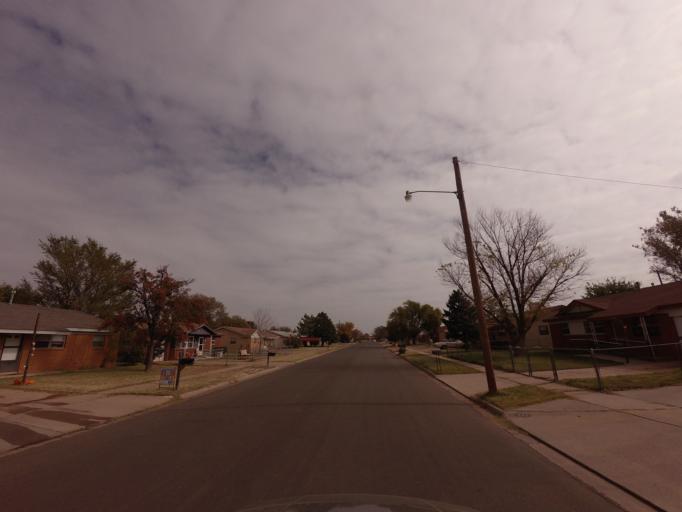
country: US
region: New Mexico
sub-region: Curry County
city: Clovis
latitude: 34.4299
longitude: -103.2218
